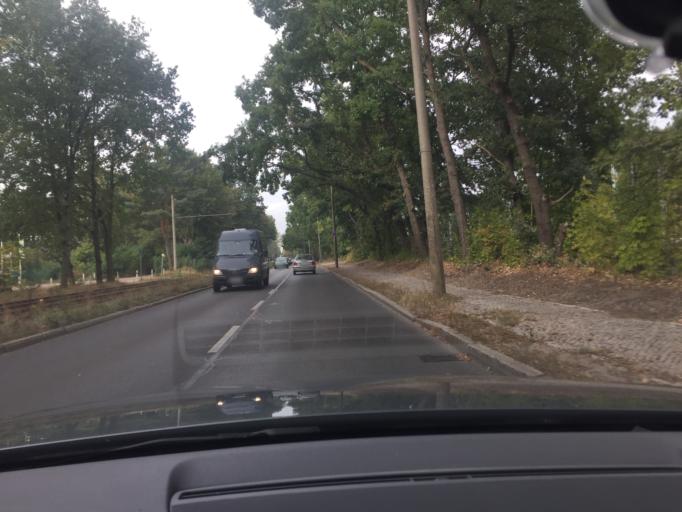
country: DE
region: Berlin
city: Friedrichshagen
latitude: 52.4565
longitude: 13.6388
